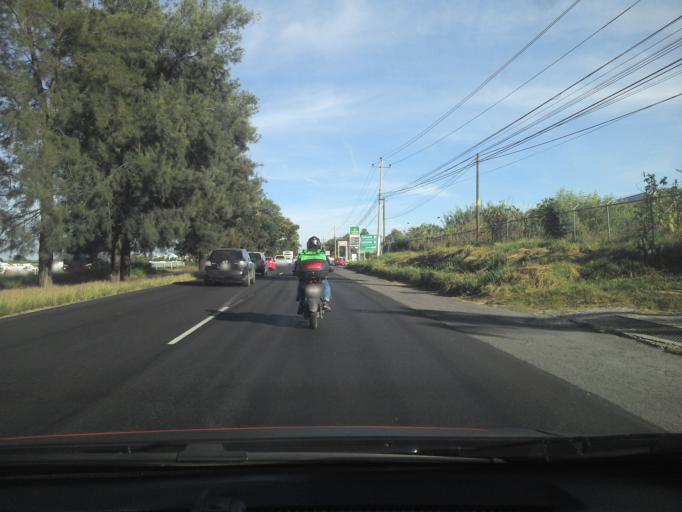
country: MX
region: Jalisco
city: Nuevo Mexico
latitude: 20.7189
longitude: -103.4855
